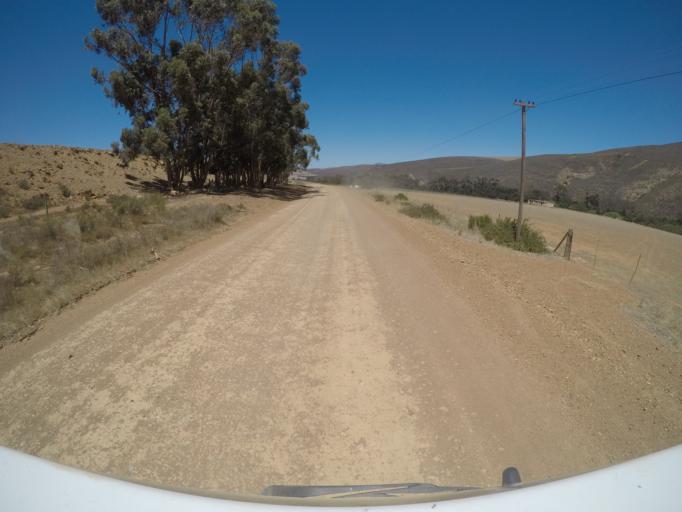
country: ZA
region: Western Cape
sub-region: Overberg District Municipality
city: Caledon
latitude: -34.1285
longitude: 19.2394
